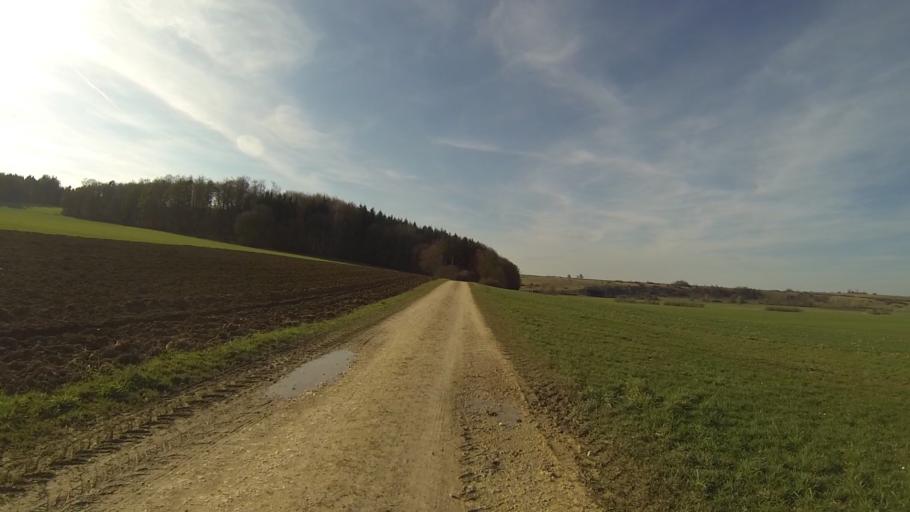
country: DE
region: Baden-Wuerttemberg
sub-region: Regierungsbezirk Stuttgart
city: Giengen an der Brenz
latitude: 48.5909
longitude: 10.2217
